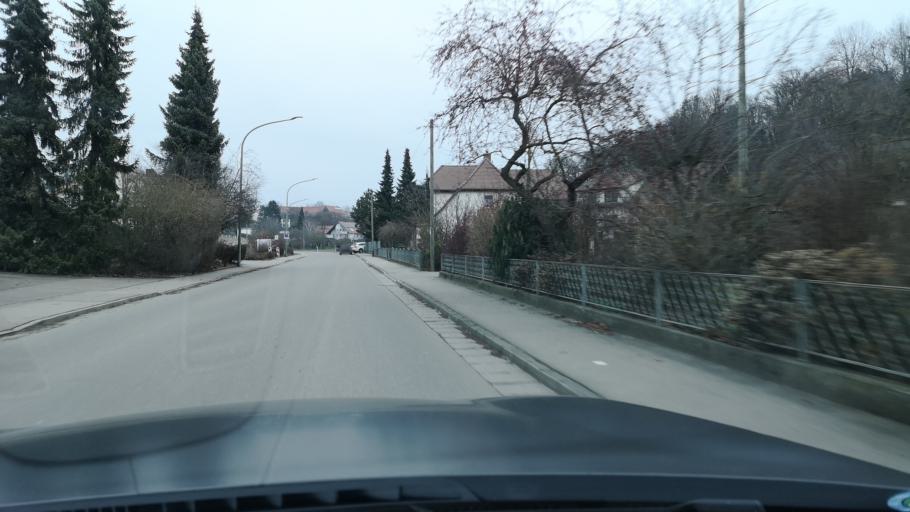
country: DE
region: Bavaria
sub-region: Swabia
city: Leipheim
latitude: 48.4220
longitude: 10.1864
